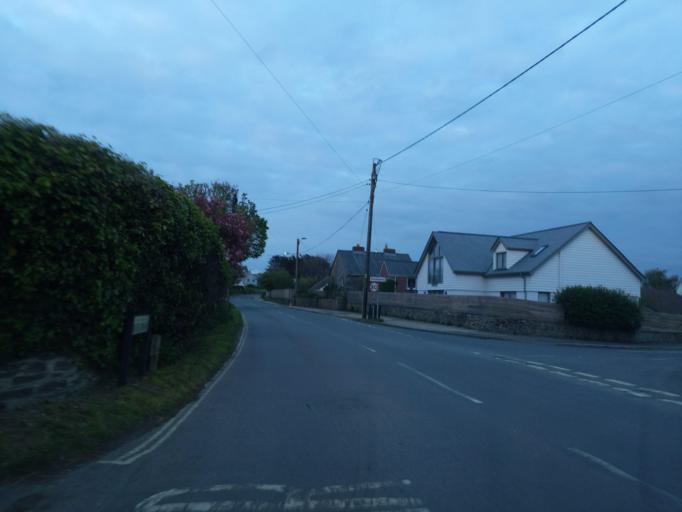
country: GB
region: England
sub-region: Cornwall
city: Polzeath
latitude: 50.5503
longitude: -4.9021
